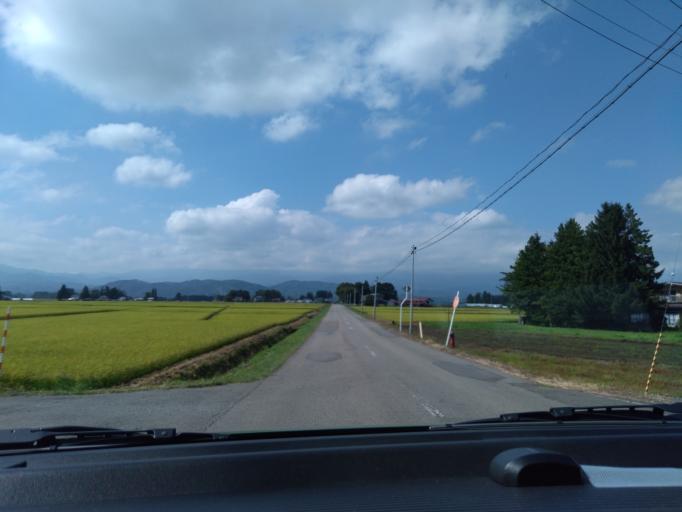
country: JP
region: Iwate
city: Shizukuishi
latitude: 39.6724
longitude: 140.9676
